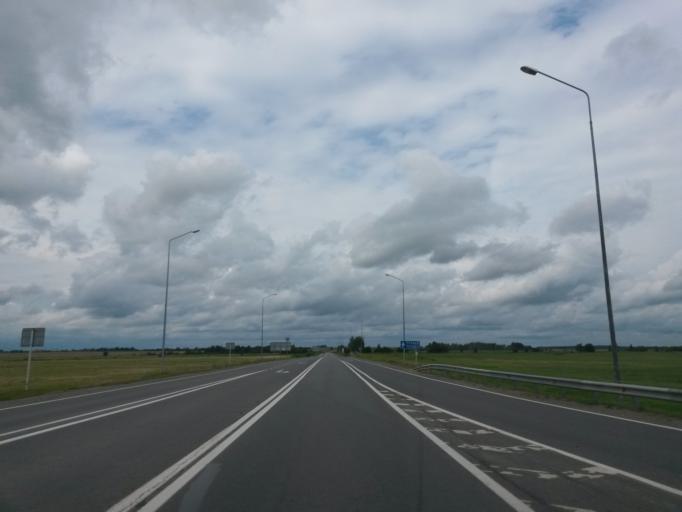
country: RU
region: Jaroslavl
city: Yaroslavl
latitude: 57.7400
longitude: 39.8917
